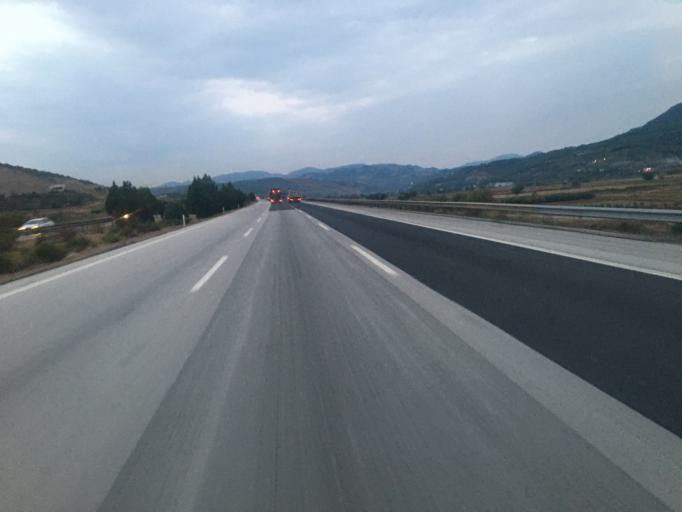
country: TR
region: Osmaniye
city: Osmaniye
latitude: 37.1499
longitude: 36.3427
